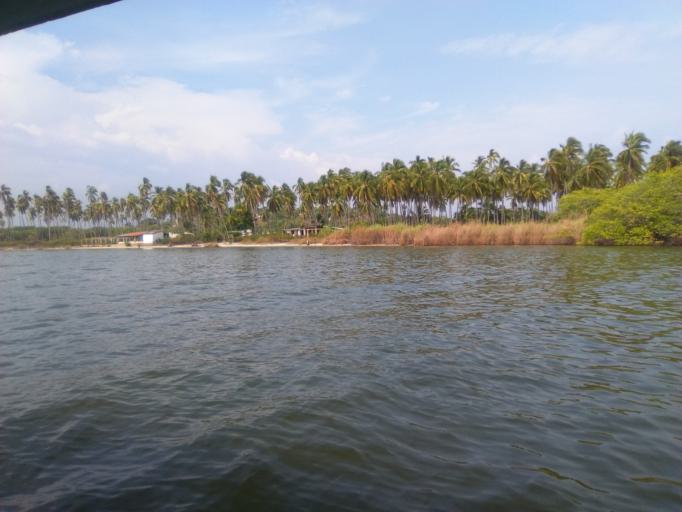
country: MX
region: Guerrero
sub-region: Coyuca de Benitez
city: Colonia Luces en el Mar
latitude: 16.9018
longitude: -99.9686
